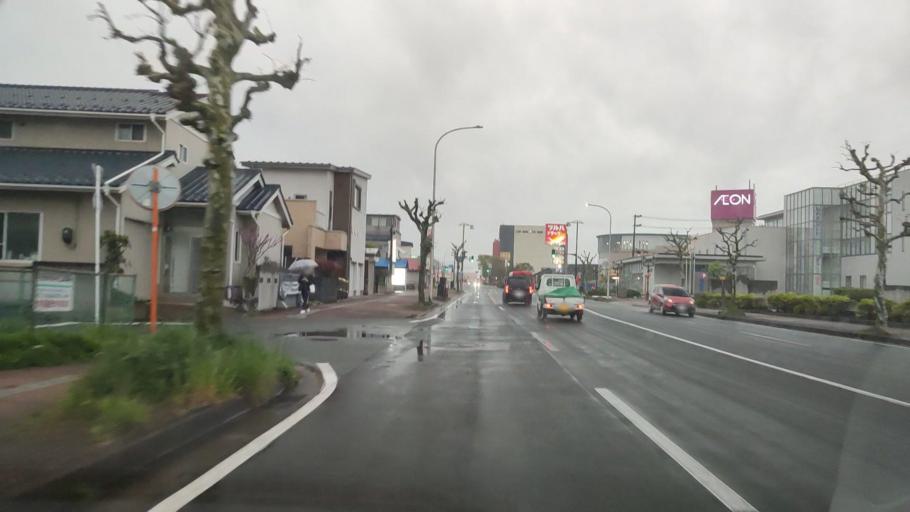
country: JP
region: Akita
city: Akita
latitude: 39.7055
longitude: 140.1120
